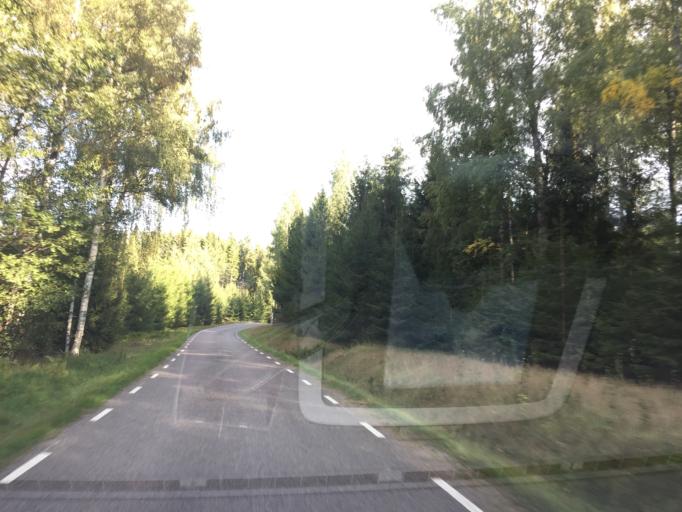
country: SE
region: Soedermanland
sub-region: Vingakers Kommun
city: Vingaker
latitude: 59.0092
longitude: 15.7121
